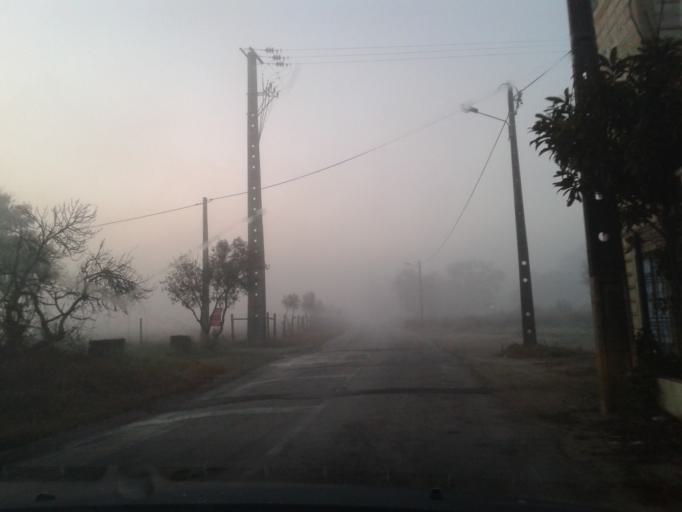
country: PT
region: Setubal
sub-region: Palmela
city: Palmela
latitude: 38.6001
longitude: -8.8970
